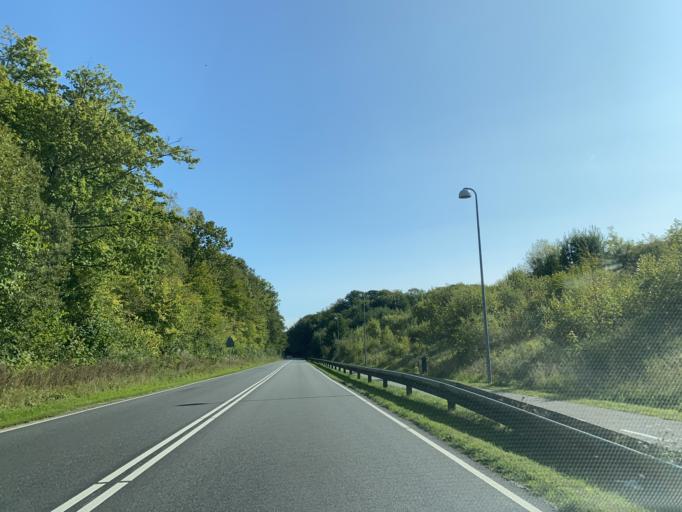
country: DK
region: South Denmark
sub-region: Aabenraa Kommune
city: Aabenraa
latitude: 55.0602
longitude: 9.3870
